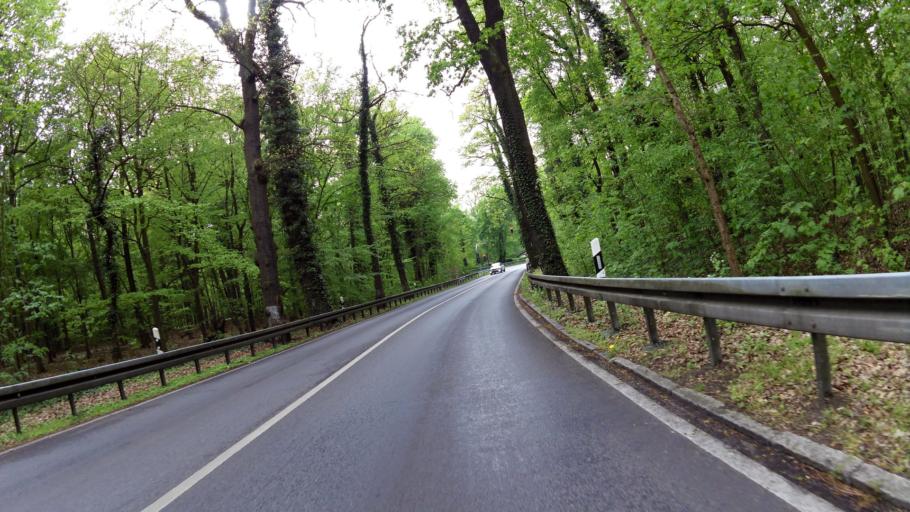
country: DE
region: Brandenburg
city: Konigs Wusterhausen
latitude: 52.2919
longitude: 13.6484
